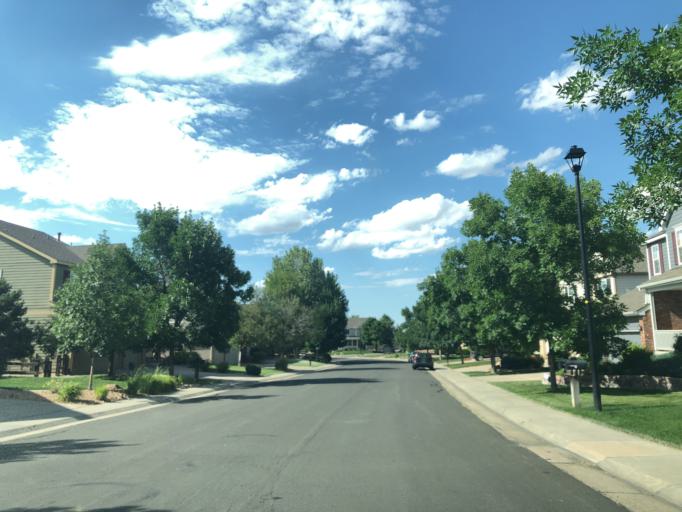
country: US
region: Colorado
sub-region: Arapahoe County
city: Dove Valley
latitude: 39.5969
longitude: -104.7751
